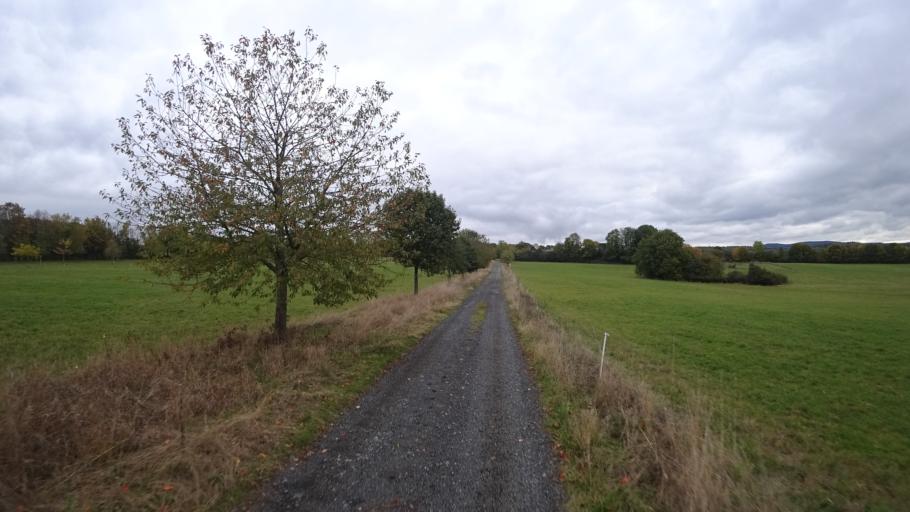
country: DE
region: Rheinland-Pfalz
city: Goddert
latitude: 50.5557
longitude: 7.7317
